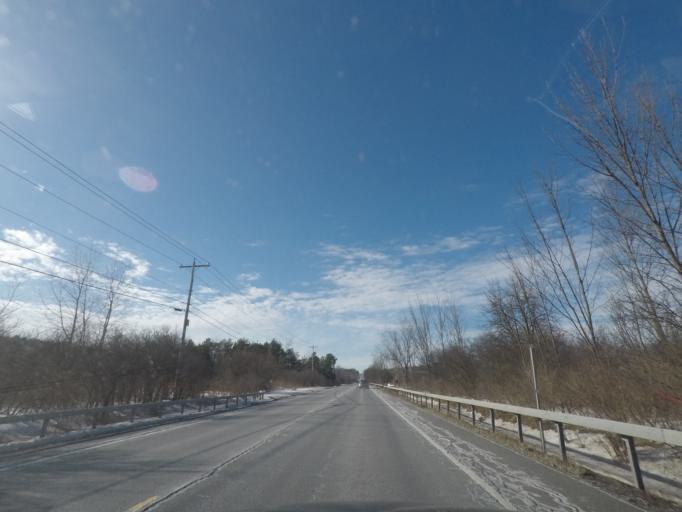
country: US
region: New York
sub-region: Albany County
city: Altamont
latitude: 42.7434
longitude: -74.0264
